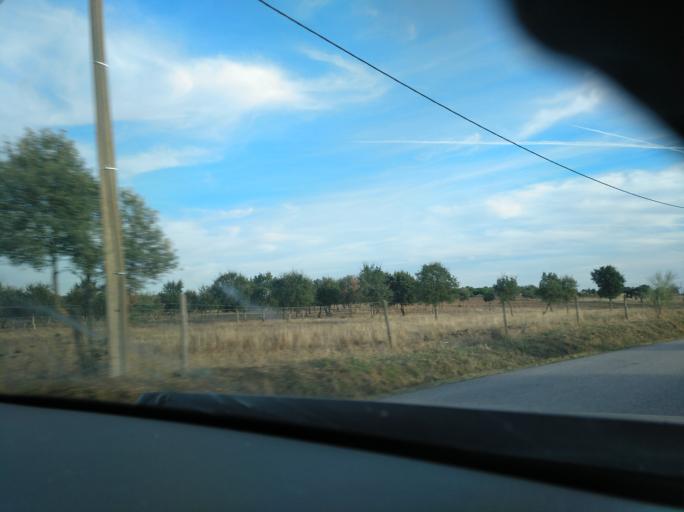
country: PT
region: Evora
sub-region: Arraiolos
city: Arraiolos
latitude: 38.8474
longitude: -7.8288
